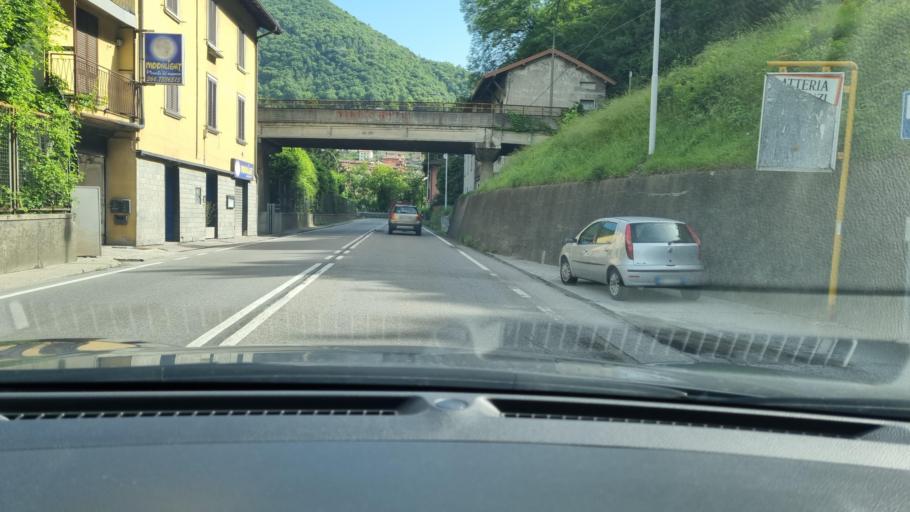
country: IT
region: Lombardy
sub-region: Provincia di Bergamo
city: Ubiale
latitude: 45.7783
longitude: 9.6137
